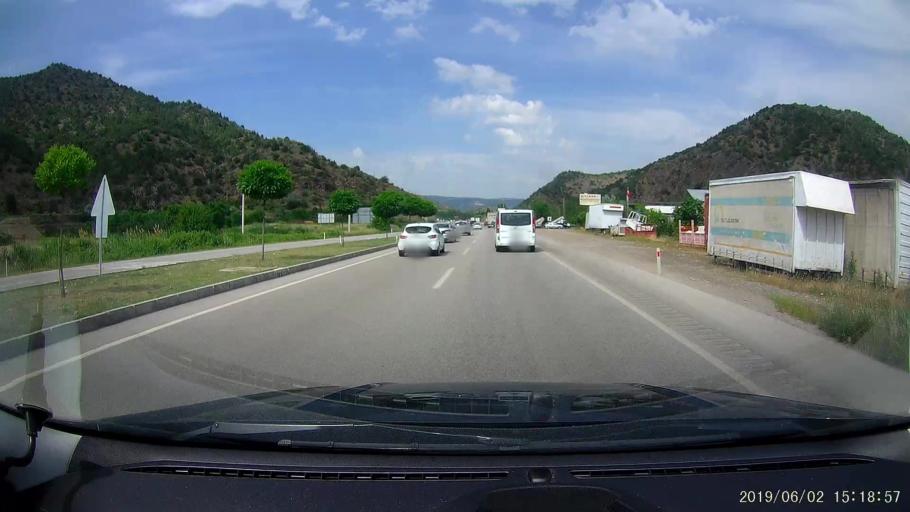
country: TR
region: Corum
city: Osmancik
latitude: 40.9662
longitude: 34.9037
